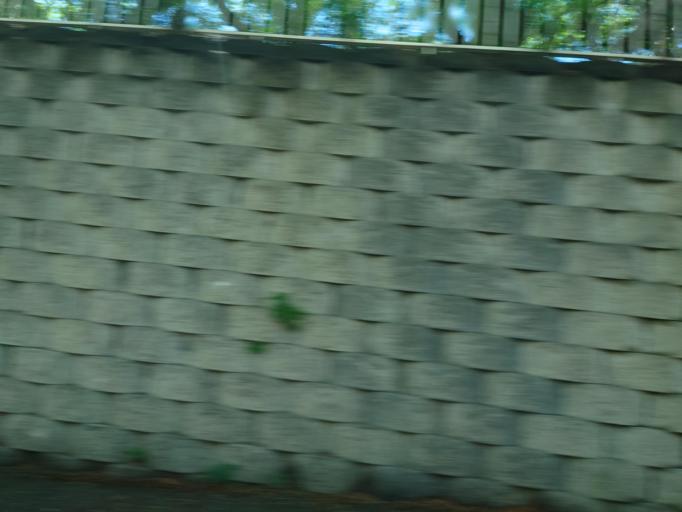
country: NC
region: South Province
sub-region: Noumea
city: Noumea
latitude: -22.2719
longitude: 166.4509
